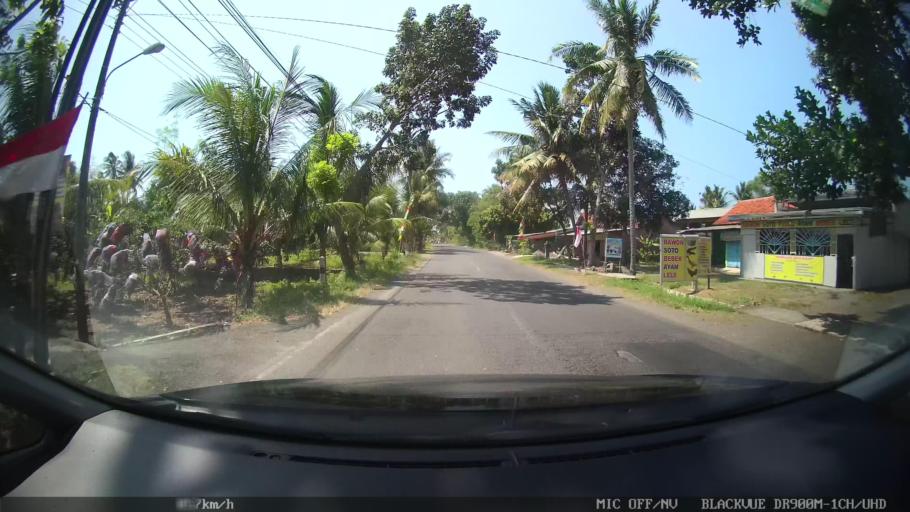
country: ID
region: Daerah Istimewa Yogyakarta
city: Srandakan
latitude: -7.9123
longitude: 110.0918
